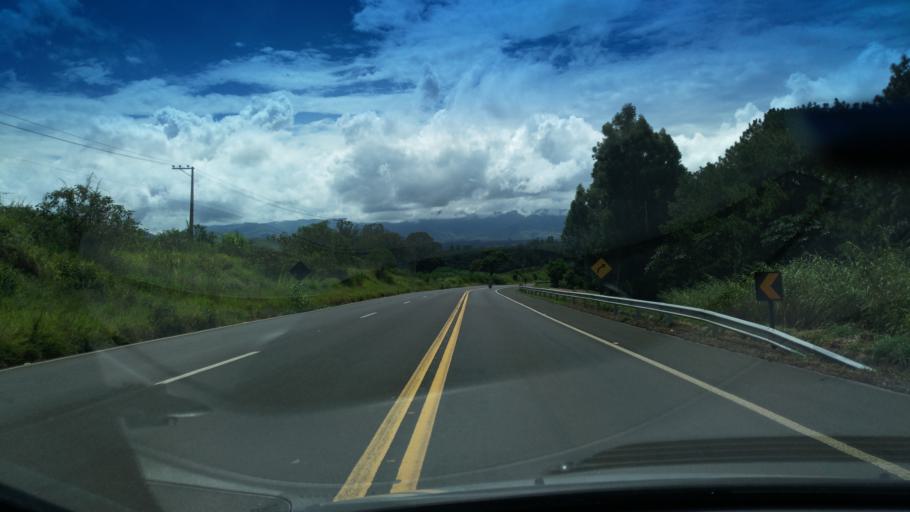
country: BR
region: Sao Paulo
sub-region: Santo Antonio Do Jardim
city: Espirito Santo do Pinhal
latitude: -22.1356
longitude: -46.7016
